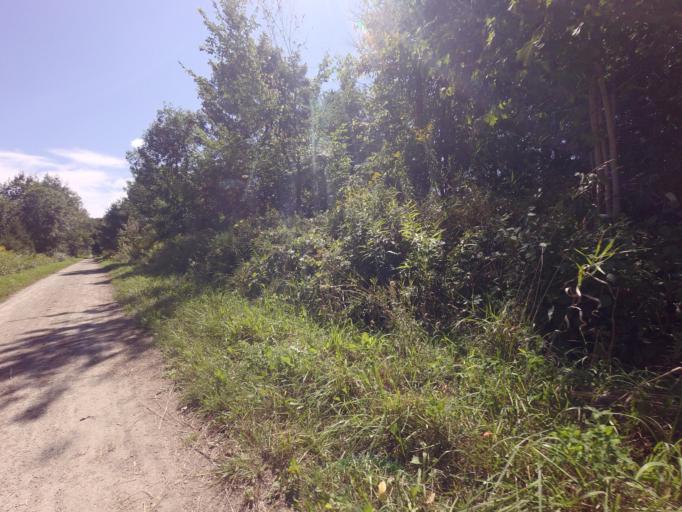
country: CA
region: Ontario
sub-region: Wellington County
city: Guelph
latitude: 43.7387
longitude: -80.3526
